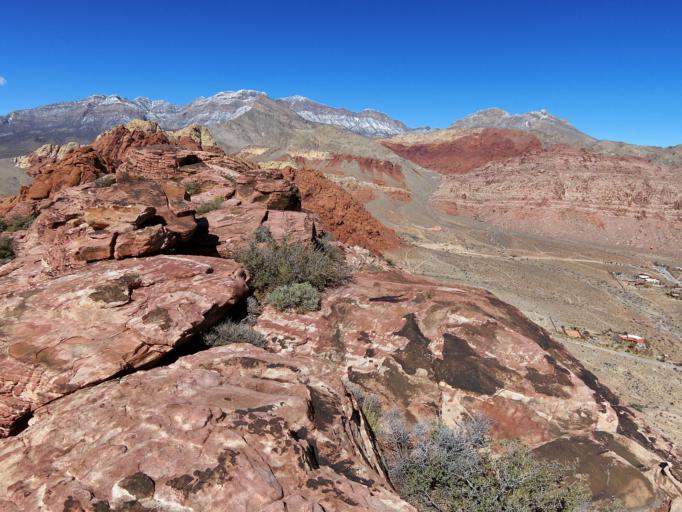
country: US
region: Nevada
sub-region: Clark County
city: Summerlin South
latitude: 36.1468
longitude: -115.4247
